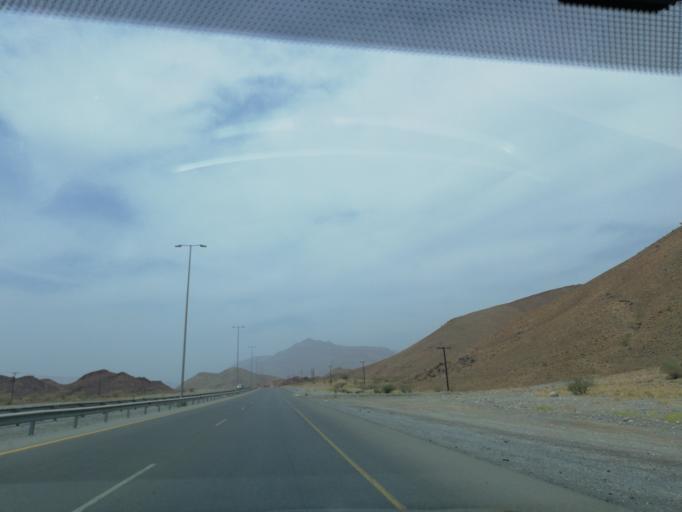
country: OM
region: Muhafazat ad Dakhiliyah
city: Izki
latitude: 22.8845
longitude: 57.7014
